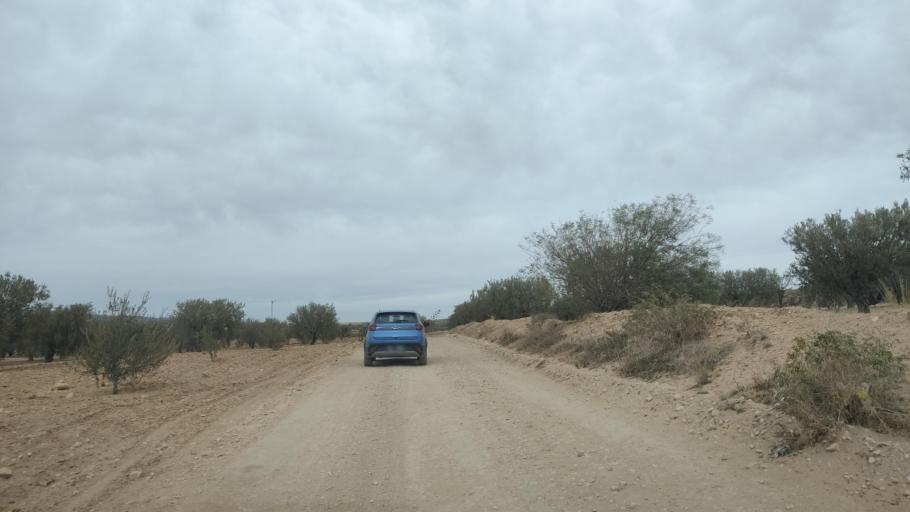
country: TN
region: Al Qasrayn
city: Kasserine
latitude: 35.2486
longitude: 8.9203
